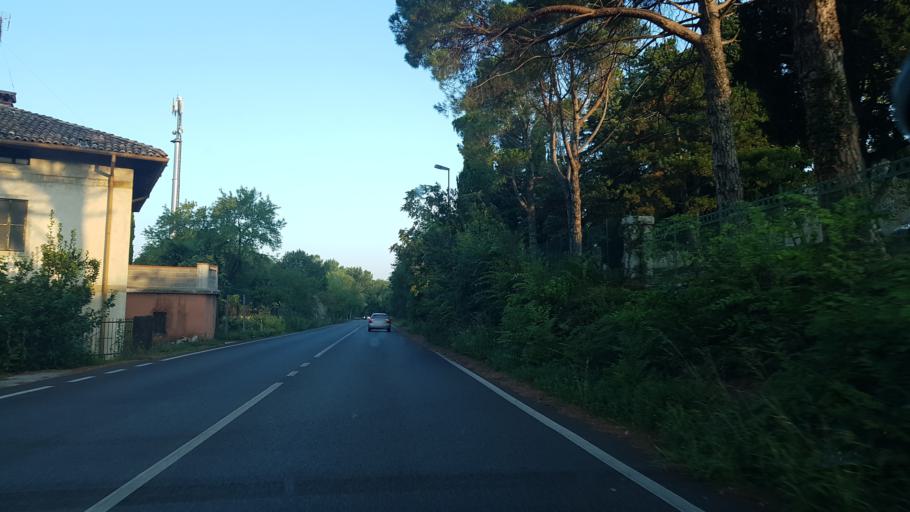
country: IT
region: Friuli Venezia Giulia
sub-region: Provincia di Trieste
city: Duino
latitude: 45.7892
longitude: 13.5902
